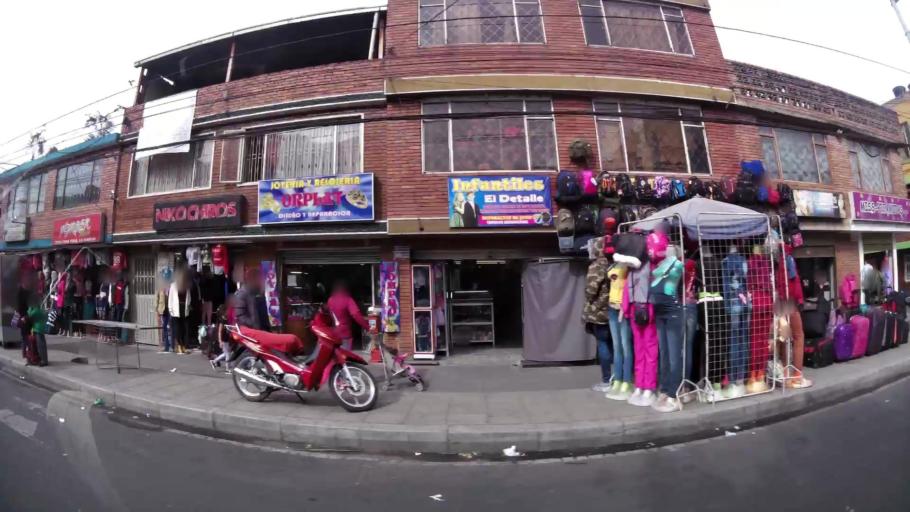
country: CO
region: Cundinamarca
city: Soacha
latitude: 4.6368
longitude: -74.1646
